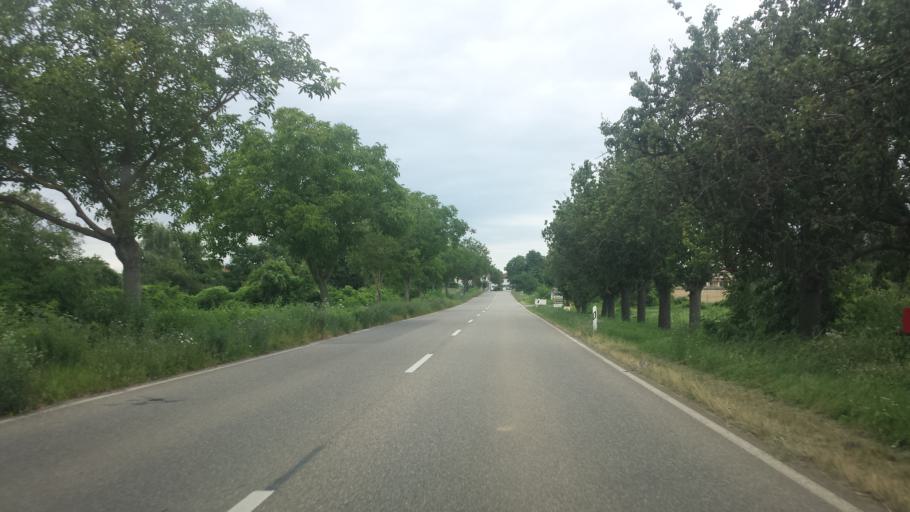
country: DE
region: Rheinland-Pfalz
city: Meckenheim
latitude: 49.3969
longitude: 8.2431
